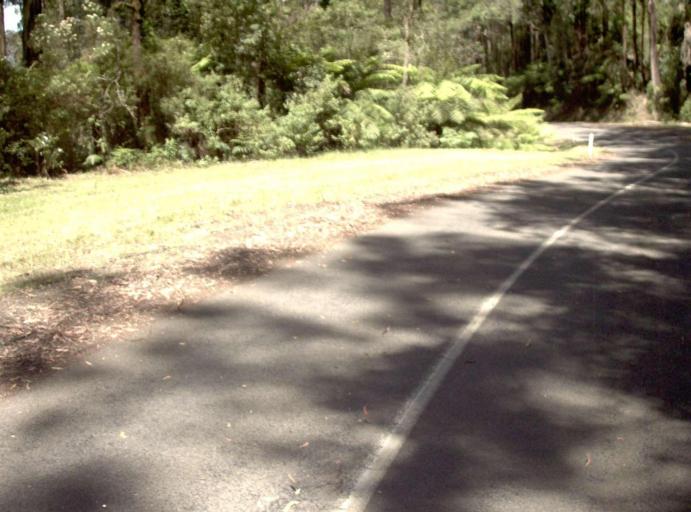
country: AU
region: Victoria
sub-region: Yarra Ranges
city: Millgrove
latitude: -37.7166
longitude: 145.7155
